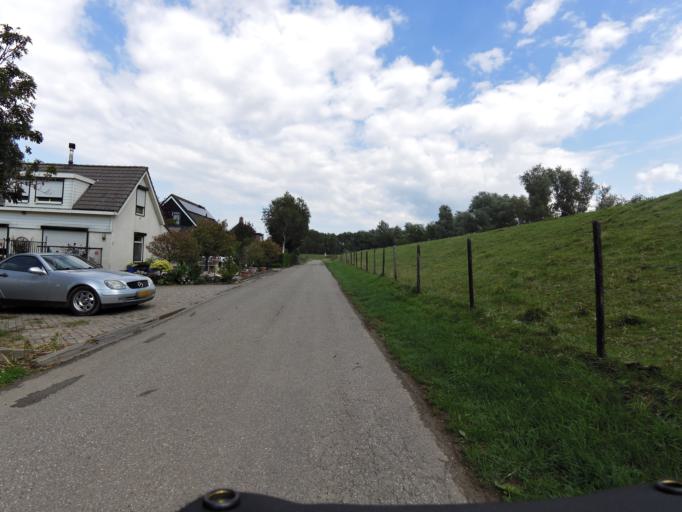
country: NL
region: South Holland
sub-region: Gemeente Strijen
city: Strijen
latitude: 51.7221
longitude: 4.6154
